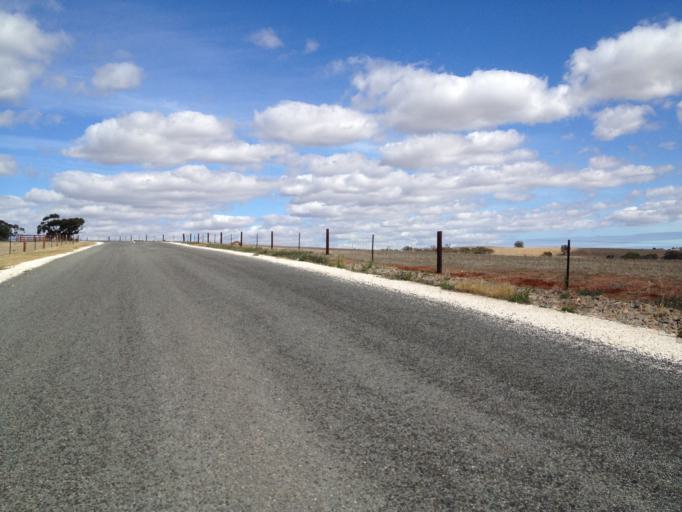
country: AU
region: South Australia
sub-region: Barossa
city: Lyndoch
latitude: -34.6286
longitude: 138.8313
